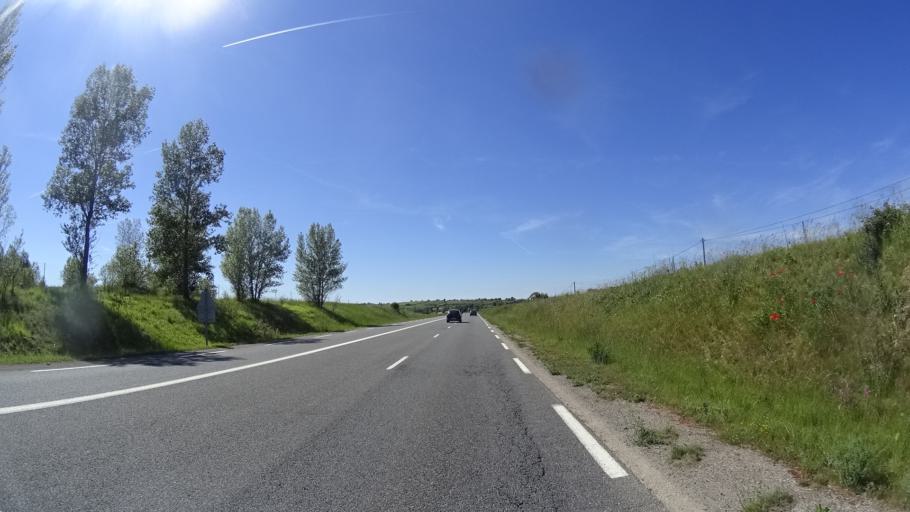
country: FR
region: Midi-Pyrenees
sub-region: Departement de l'Aveyron
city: Salles-la-Source
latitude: 44.4142
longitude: 2.4811
